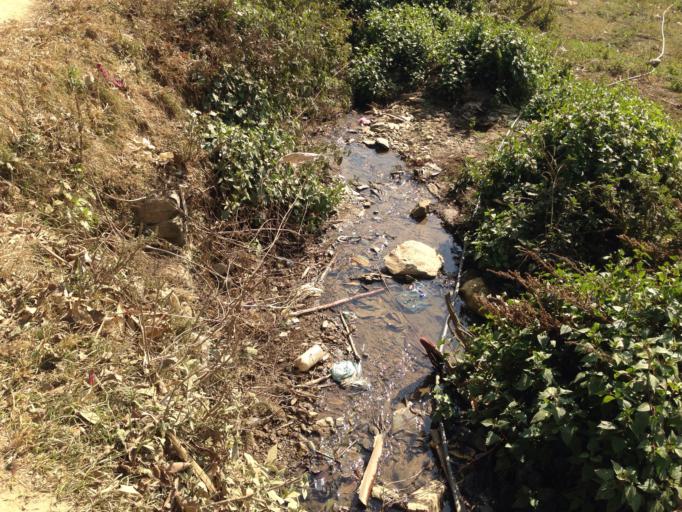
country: NP
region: Central Region
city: Kirtipur
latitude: 27.7294
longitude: 85.2659
